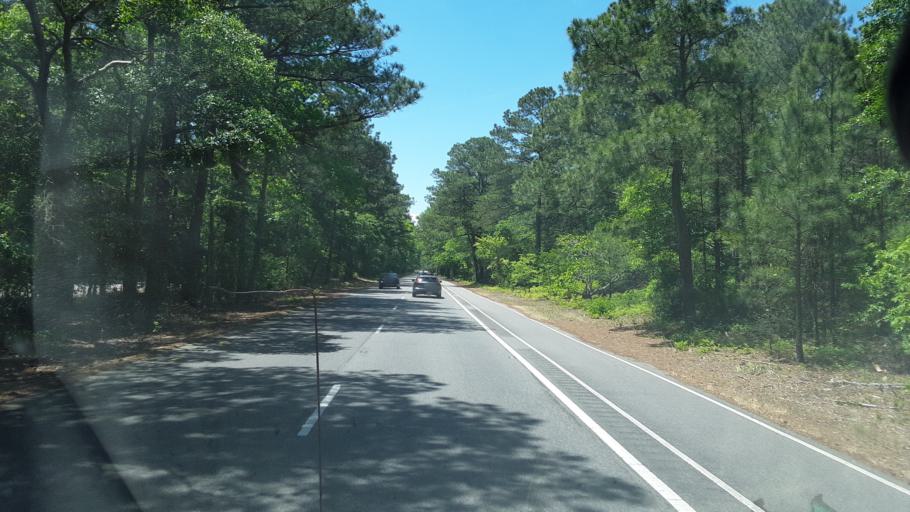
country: US
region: Virginia
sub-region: City of Virginia Beach
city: Virginia Beach
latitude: 36.9200
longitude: -76.0276
